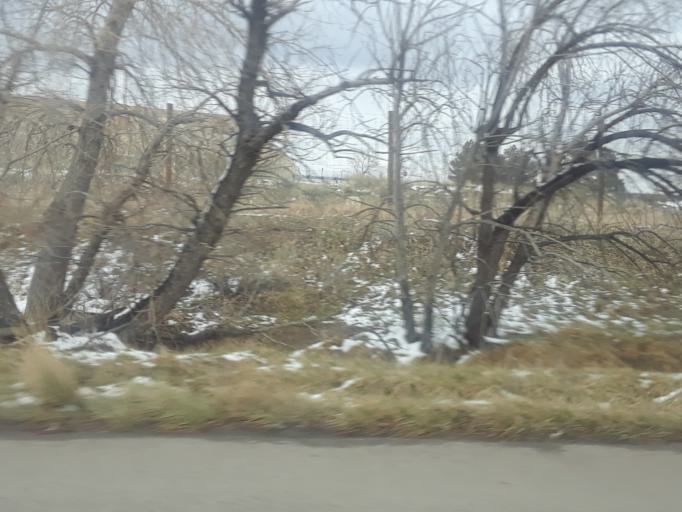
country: US
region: Colorado
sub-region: Jefferson County
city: Golden
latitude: 39.7323
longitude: -105.2122
